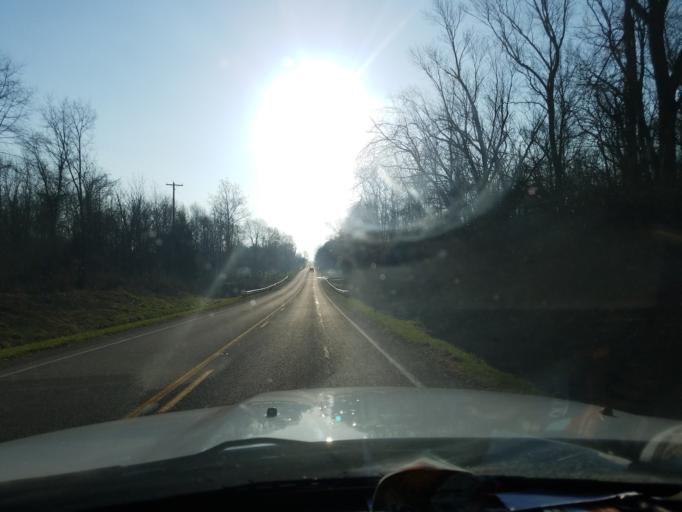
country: US
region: Indiana
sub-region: Vigo County
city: Seelyville
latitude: 39.3902
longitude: -87.2649
